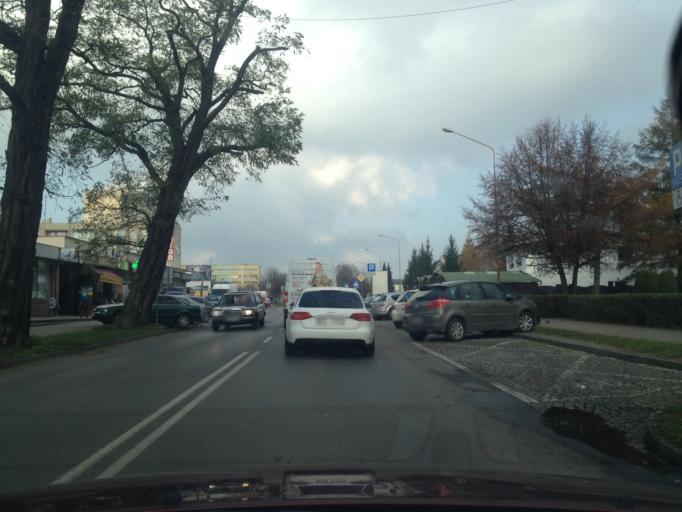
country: PL
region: Lower Silesian Voivodeship
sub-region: Powiat zgorzelecki
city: Zgorzelec
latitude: 51.1560
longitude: 15.0074
